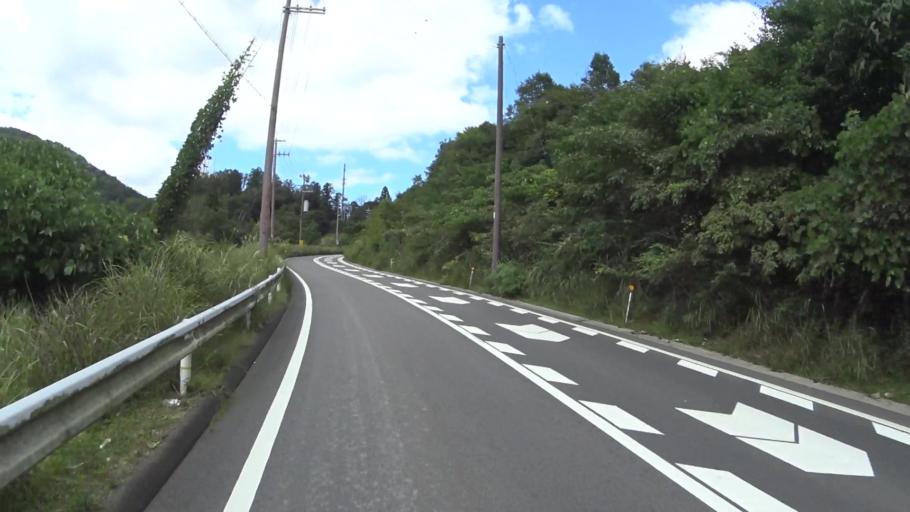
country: JP
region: Shiga Prefecture
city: Otsu-shi
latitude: 34.9287
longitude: 135.8880
